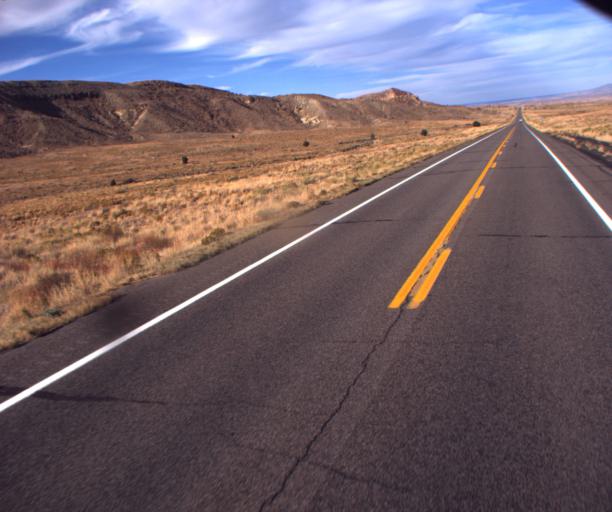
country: US
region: New Mexico
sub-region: San Juan County
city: Shiprock
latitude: 36.9290
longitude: -109.0811
